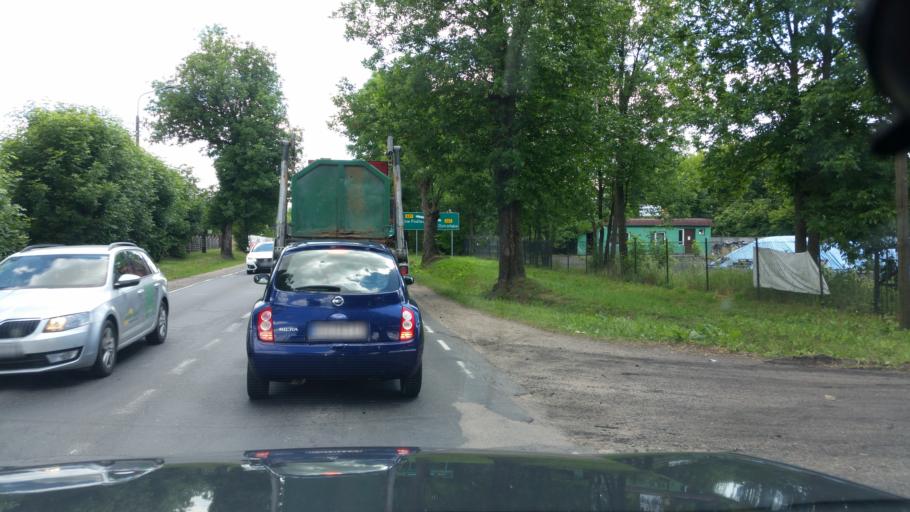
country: PL
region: Masovian Voivodeship
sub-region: Powiat ostrowski
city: Ostrow Mazowiecka
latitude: 52.8277
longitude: 21.8798
